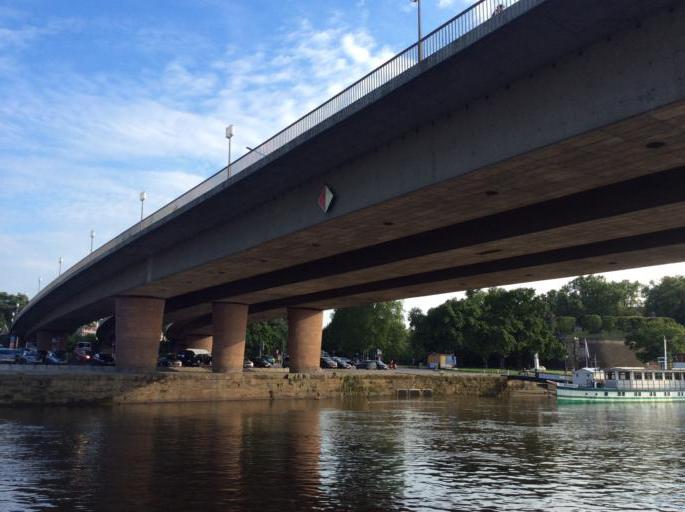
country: DE
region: Saxony
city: Dresden
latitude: 51.0545
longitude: 13.7476
